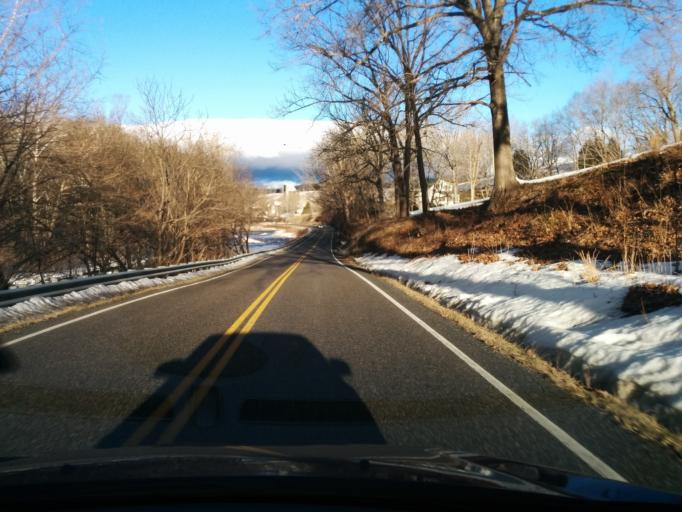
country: US
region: Virginia
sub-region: City of Lexington
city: Lexington
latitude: 37.7446
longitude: -79.5099
